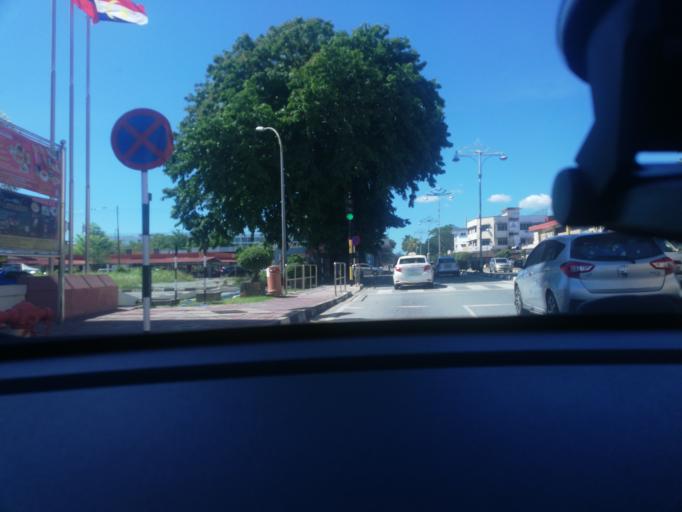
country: MY
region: Labuan
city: Victoria
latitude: 5.2782
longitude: 115.2438
